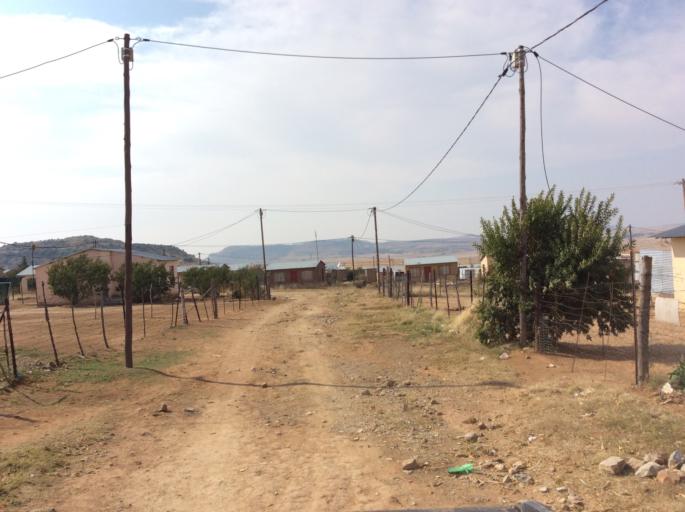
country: ZA
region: Orange Free State
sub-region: Xhariep District Municipality
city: Dewetsdorp
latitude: -29.5973
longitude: 26.6796
